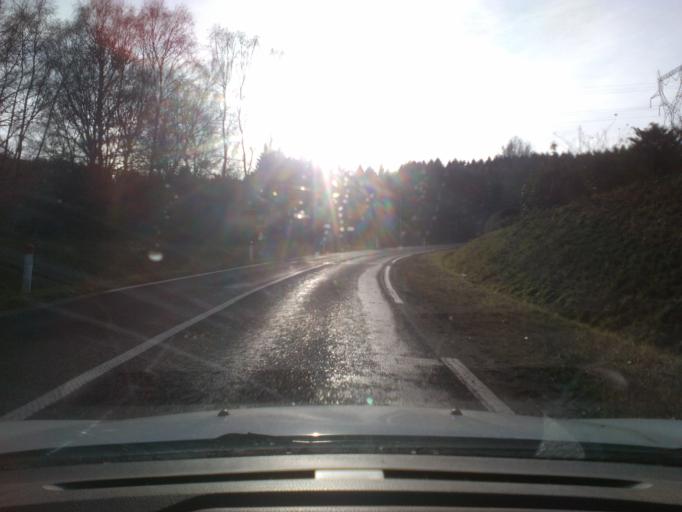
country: FR
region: Lorraine
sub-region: Departement des Vosges
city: Anould
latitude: 48.1716
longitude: 6.9272
